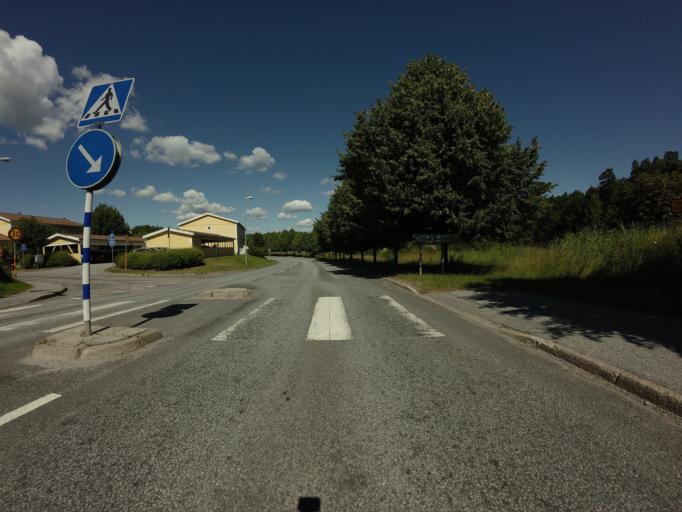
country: SE
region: Stockholm
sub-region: Upplands Vasby Kommun
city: Upplands Vaesby
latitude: 59.4612
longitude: 17.8996
